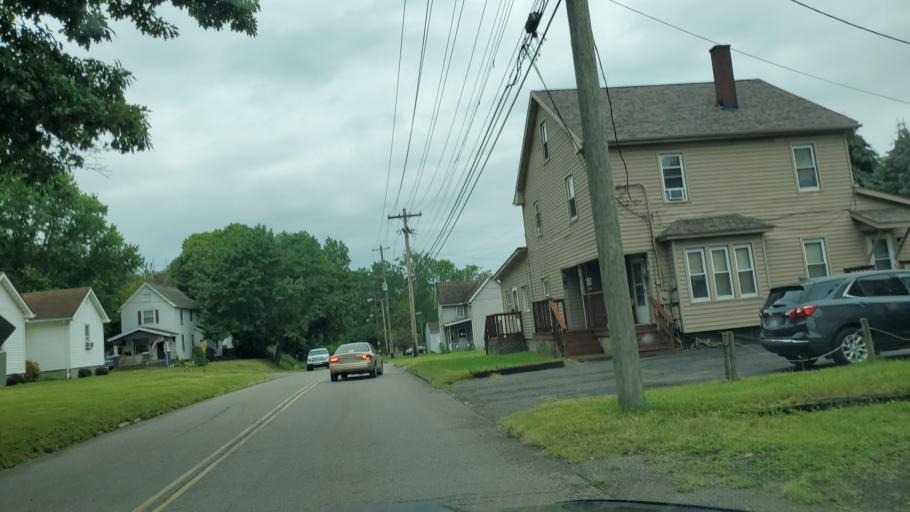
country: US
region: Ohio
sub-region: Trumbull County
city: Niles
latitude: 41.1723
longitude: -80.7491
